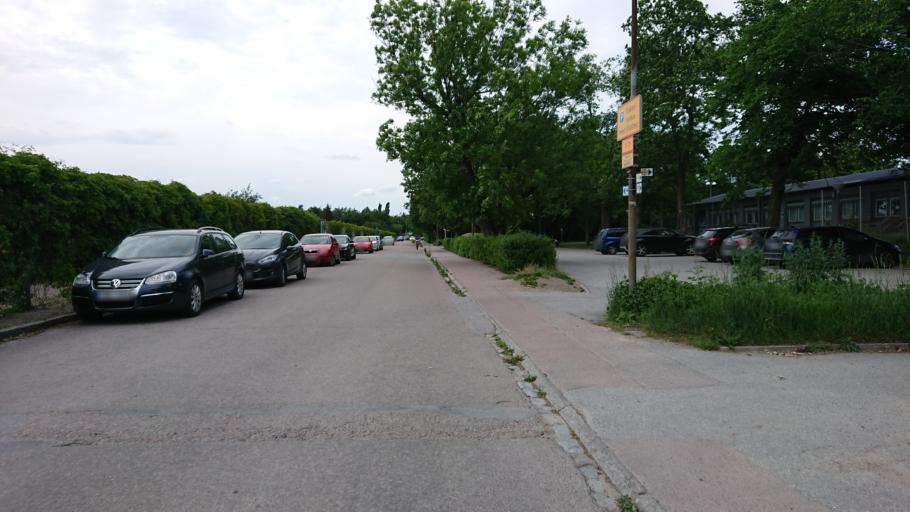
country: SE
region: Uppsala
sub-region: Uppsala Kommun
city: Gamla Uppsala
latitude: 59.8757
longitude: 17.6142
